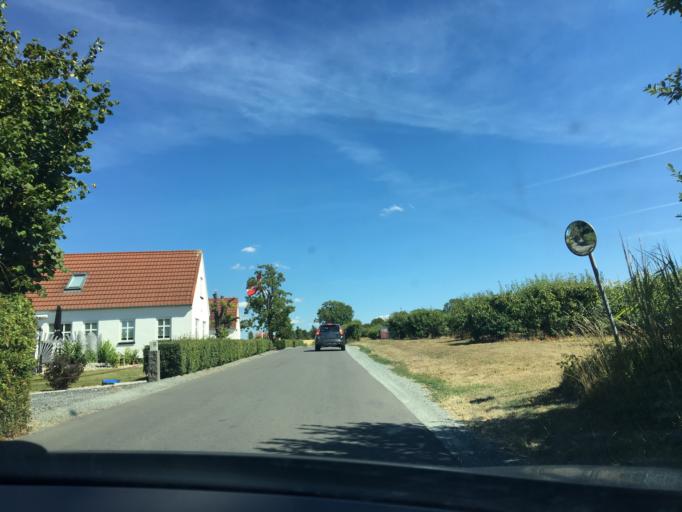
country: DK
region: South Denmark
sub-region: Middelfart Kommune
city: Norre Aby
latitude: 55.5064
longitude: 9.8818
